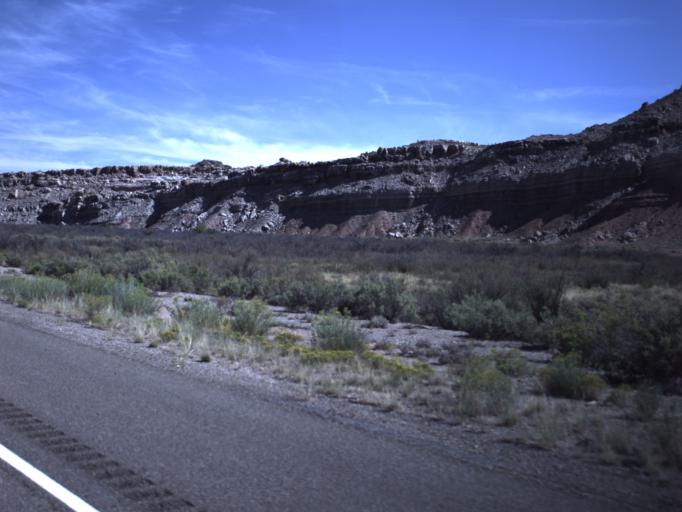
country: US
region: Utah
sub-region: Carbon County
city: East Carbon City
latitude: 38.9238
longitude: -110.4083
